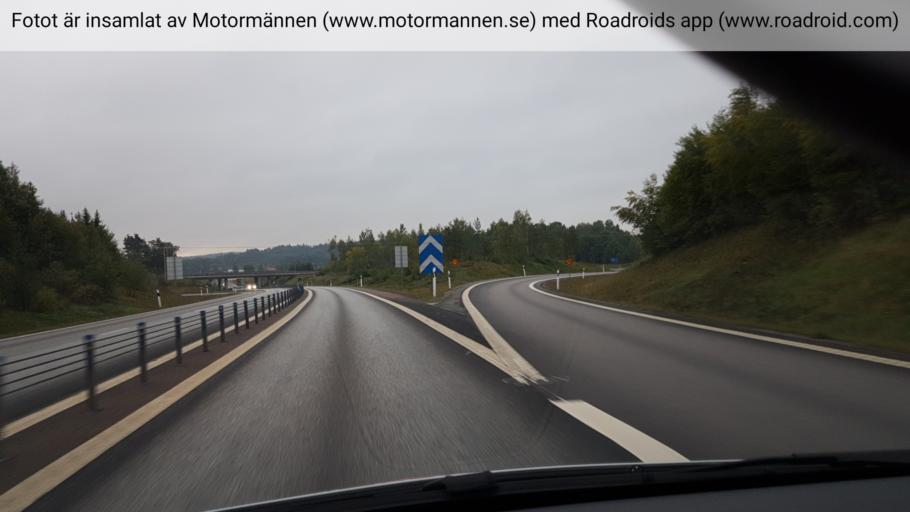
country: SE
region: Vaestmanland
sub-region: Arboga Kommun
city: Arboga
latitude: 59.4071
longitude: 15.8857
